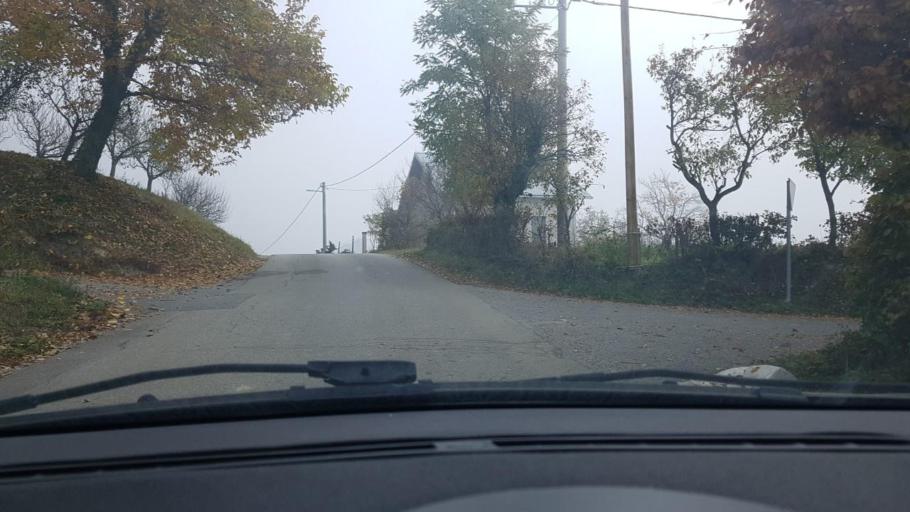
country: HR
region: Varazdinska
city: Lepoglava
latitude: 46.1567
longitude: 16.0229
